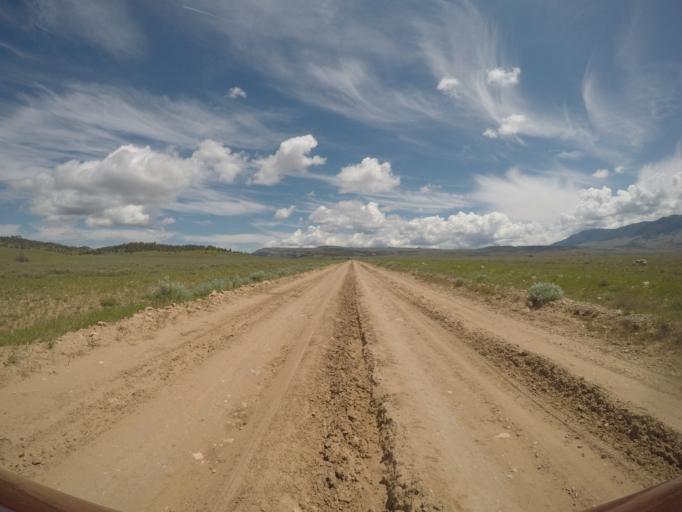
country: US
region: Montana
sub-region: Yellowstone County
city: Laurel
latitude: 45.2360
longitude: -108.6830
